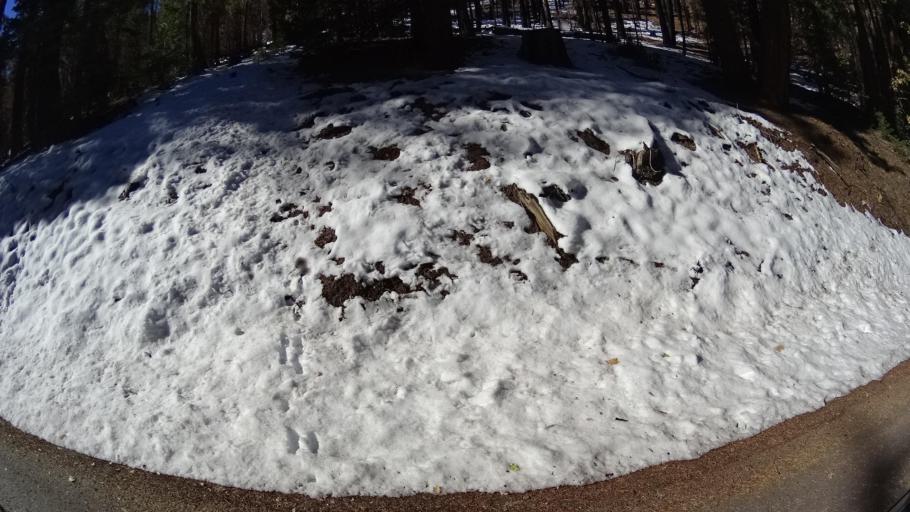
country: US
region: California
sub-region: Kern County
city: Alta Sierra
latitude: 35.7327
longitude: -118.5596
